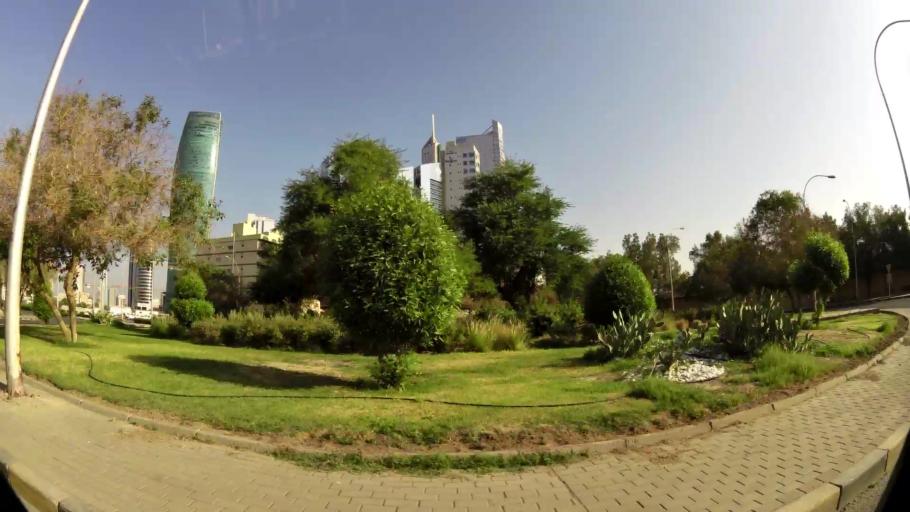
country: KW
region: Al Asimah
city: Kuwait City
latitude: 29.3712
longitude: 47.9882
